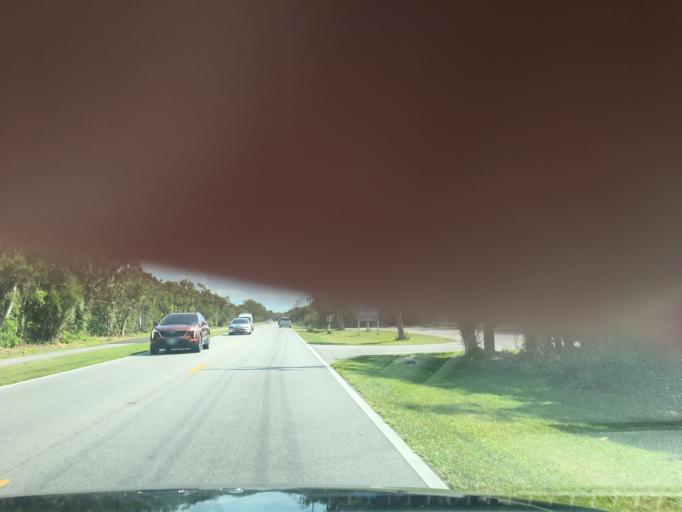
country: US
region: Florida
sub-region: Lee County
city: Saint James City
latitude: 26.4418
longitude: -82.1056
